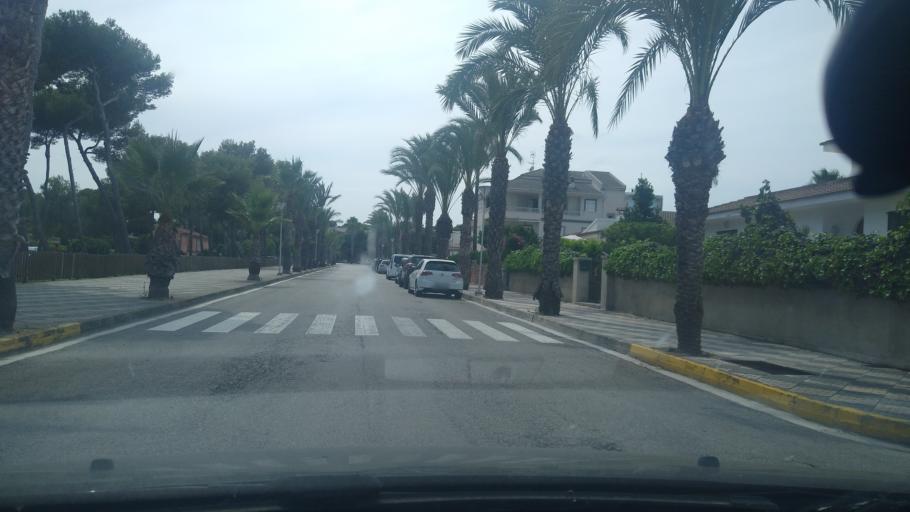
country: ES
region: Balearic Islands
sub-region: Illes Balears
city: Santa Margalida
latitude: 39.7595
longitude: 3.1620
